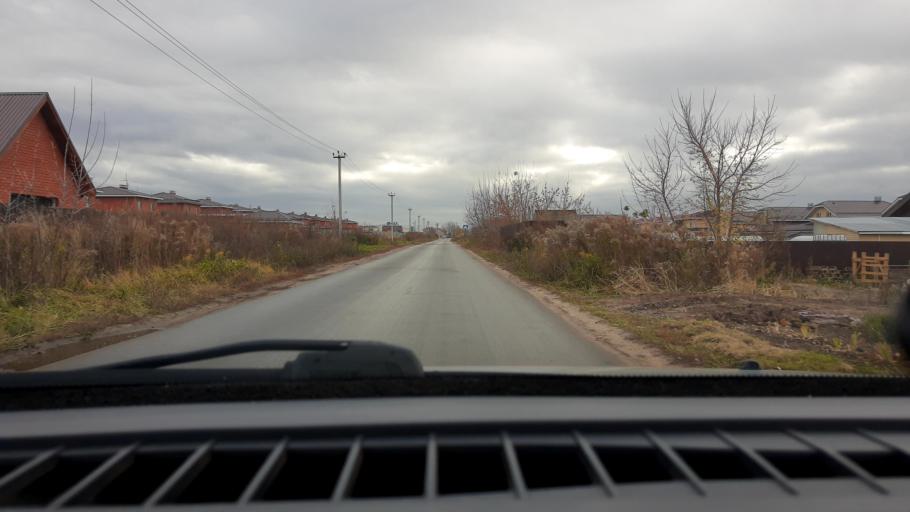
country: RU
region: Nizjnij Novgorod
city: Afonino
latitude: 56.2045
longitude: 44.1296
